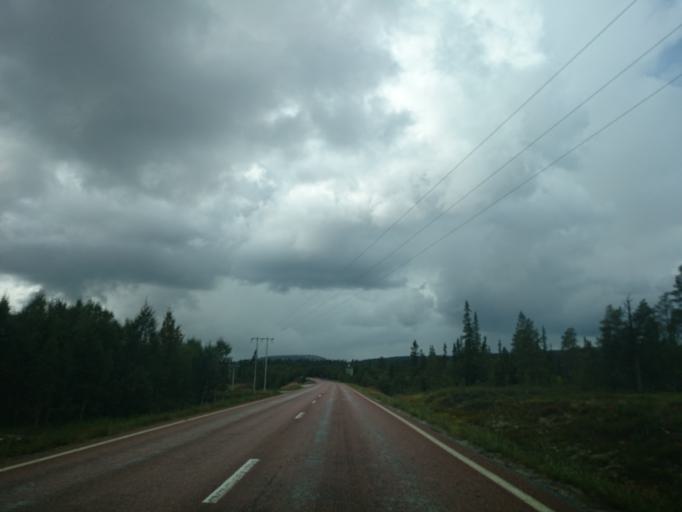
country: SE
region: Jaemtland
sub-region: Bergs Kommun
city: Hoverberg
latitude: 62.4801
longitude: 14.0549
